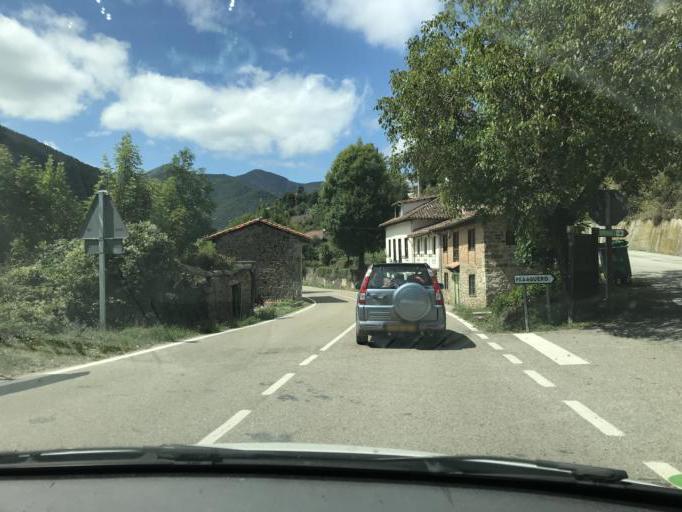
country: ES
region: Cantabria
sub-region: Provincia de Cantabria
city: Cabezon de Liebana
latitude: 43.0752
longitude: -4.5361
